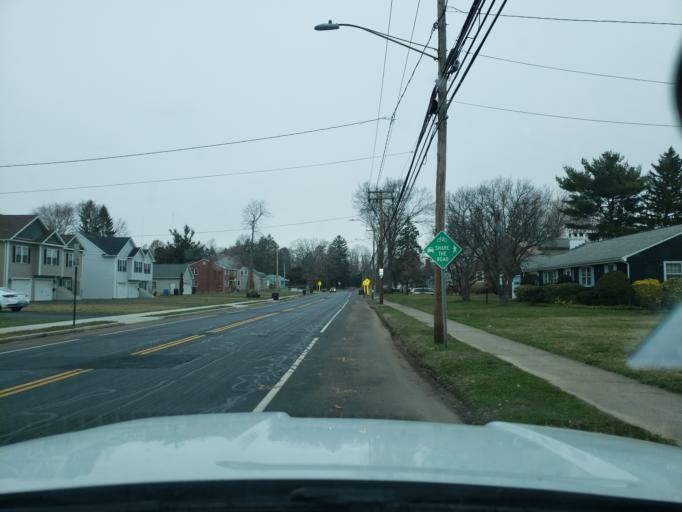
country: US
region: Connecticut
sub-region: Hartford County
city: New Britain
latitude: 41.6746
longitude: -72.8108
